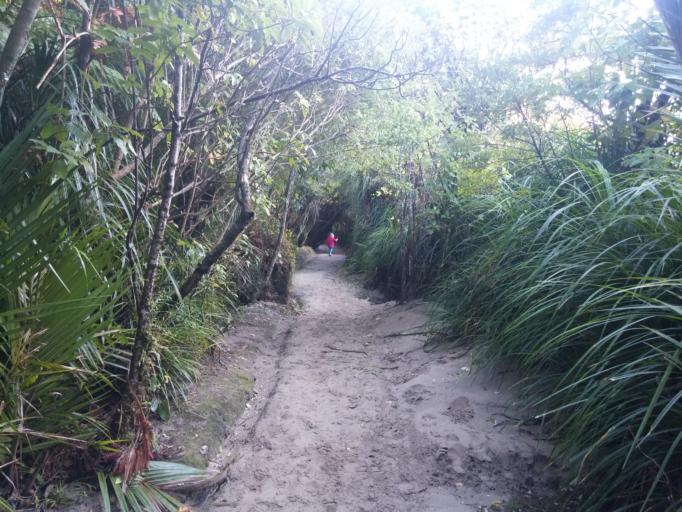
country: NZ
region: West Coast
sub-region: Grey District
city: Greymouth
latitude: -42.1095
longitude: 171.3448
